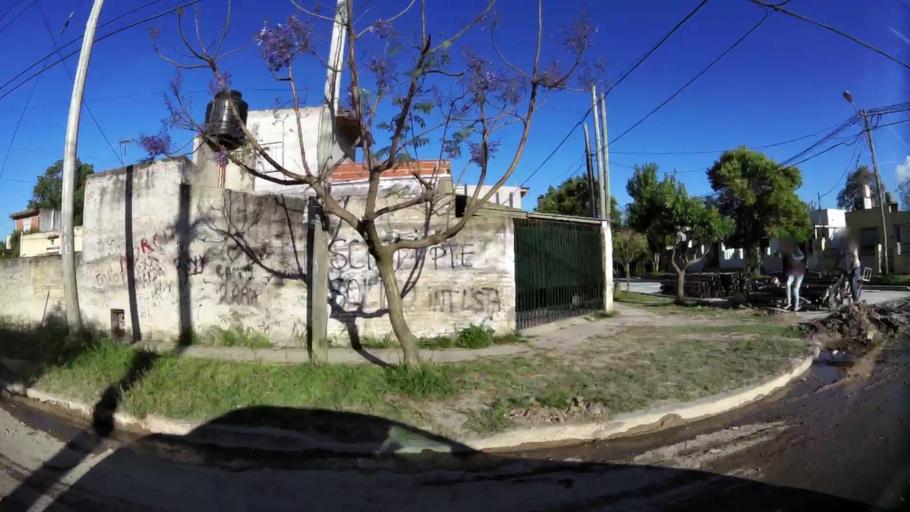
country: AR
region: Buenos Aires
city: Ituzaingo
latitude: -34.6868
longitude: -58.6391
